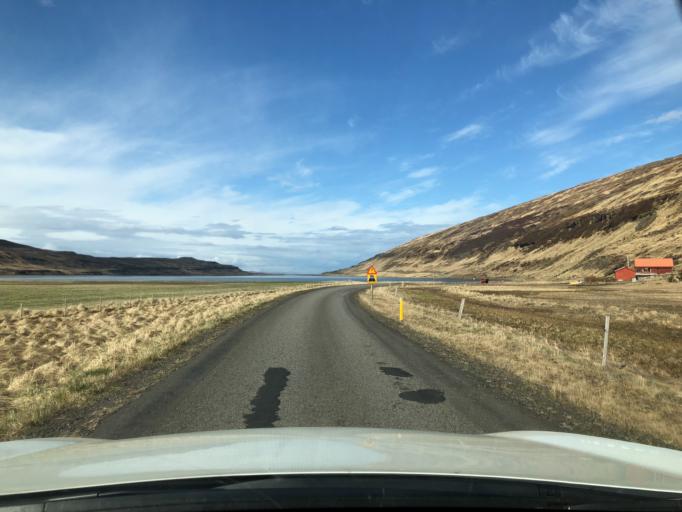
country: IS
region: West
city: Borgarnes
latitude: 65.0588
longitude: -21.5758
